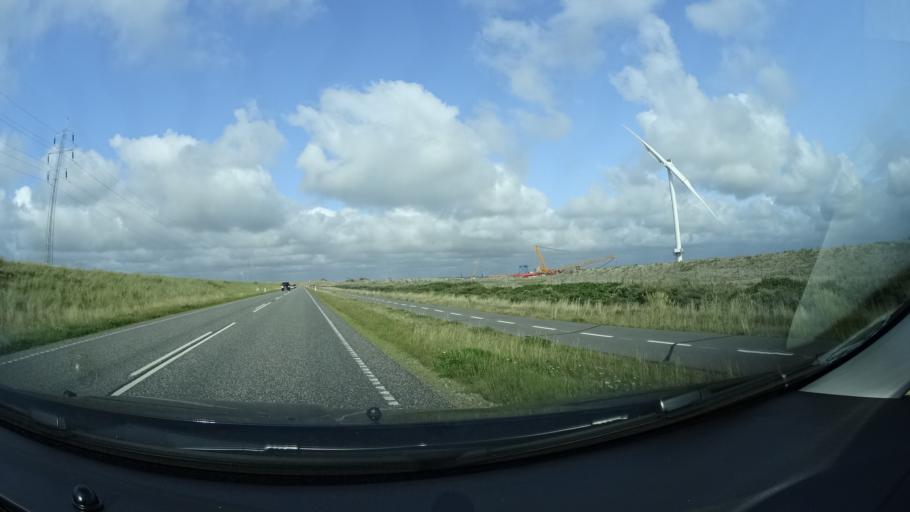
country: DK
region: Central Jutland
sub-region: Lemvig Kommune
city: Thyboron
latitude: 56.6745
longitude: 8.2169
